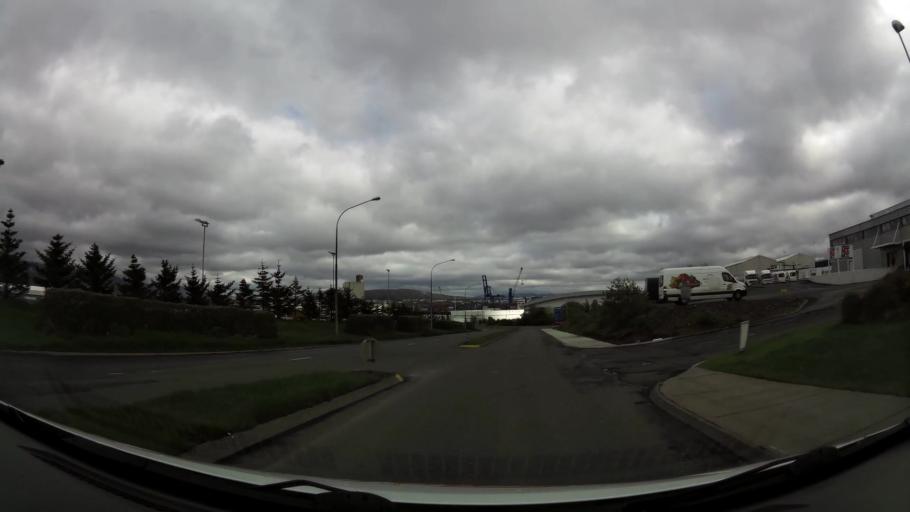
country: IS
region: Capital Region
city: Reykjavik
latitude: 64.1512
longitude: -21.8691
